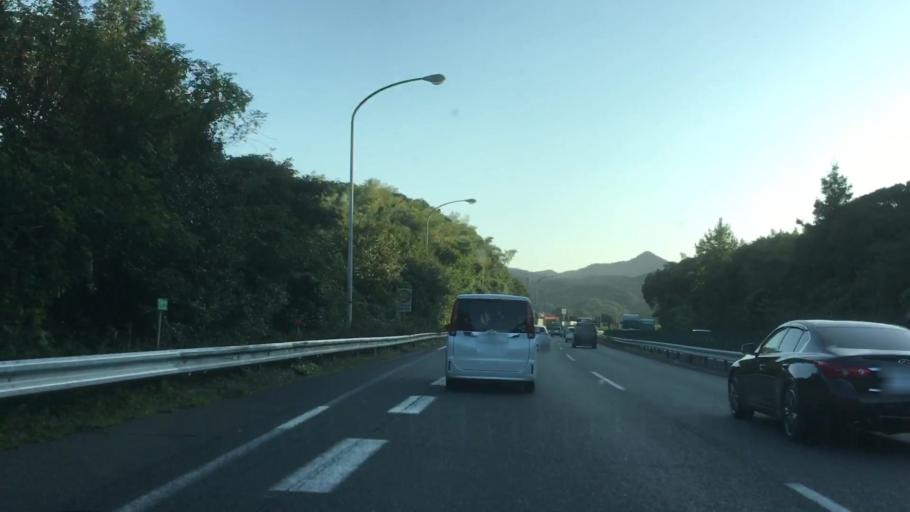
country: JP
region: Yamaguchi
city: Shimonoseki
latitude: 34.0533
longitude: 131.0062
